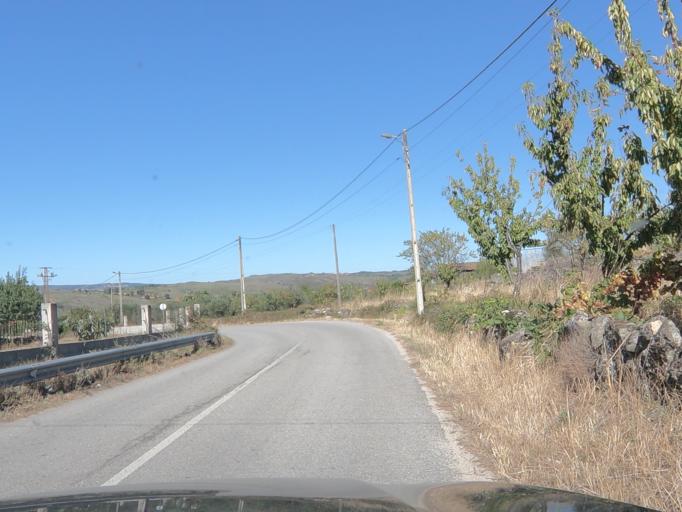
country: PT
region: Vila Real
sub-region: Valpacos
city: Valpacos
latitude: 41.6650
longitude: -7.3114
